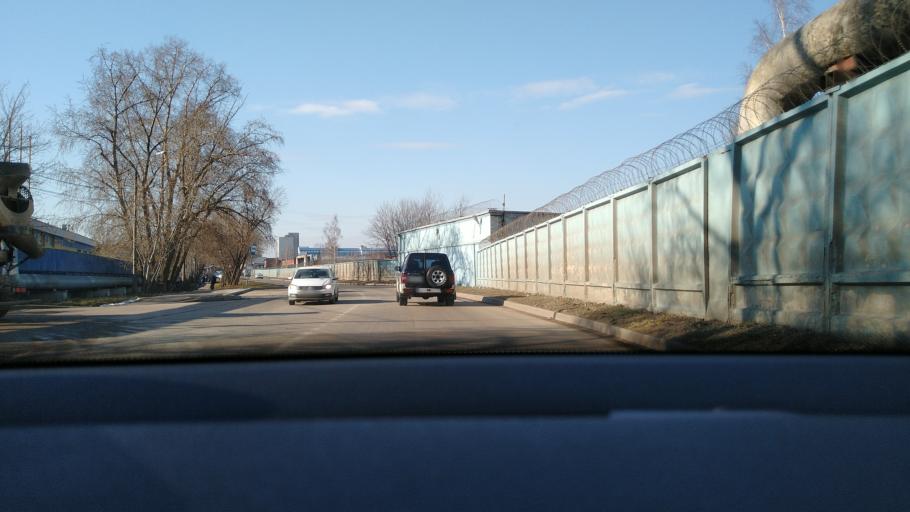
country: RU
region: Moscow
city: Khimki
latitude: 55.9008
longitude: 37.4443
